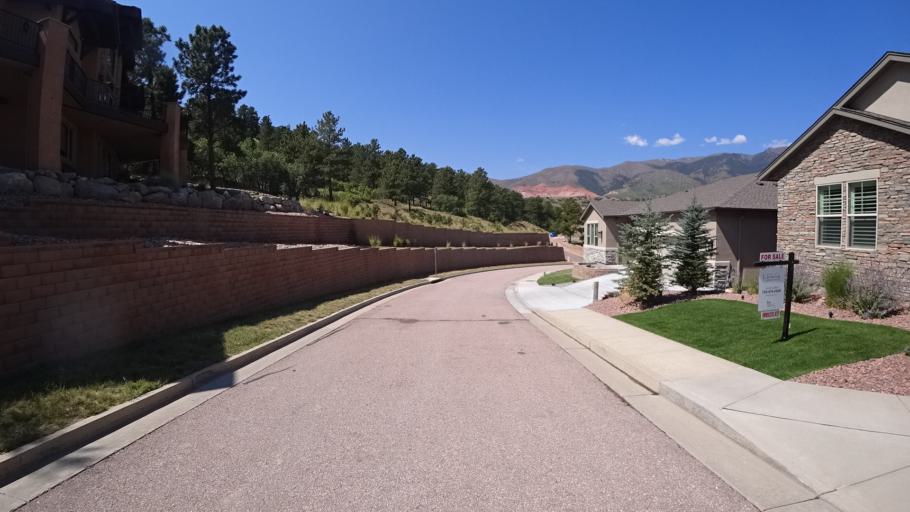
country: US
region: Colorado
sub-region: El Paso County
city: Air Force Academy
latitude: 38.9408
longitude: -104.8635
